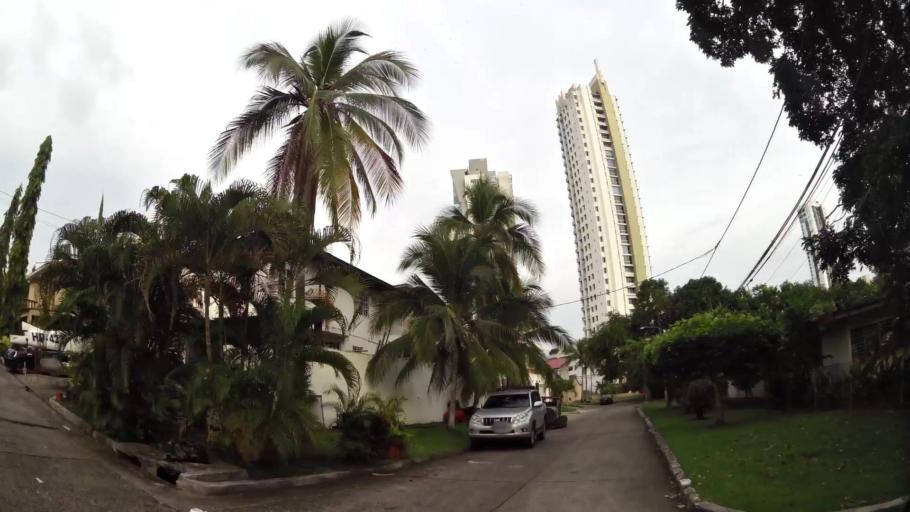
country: PA
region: Panama
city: Panama
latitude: 8.9973
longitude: -79.4995
